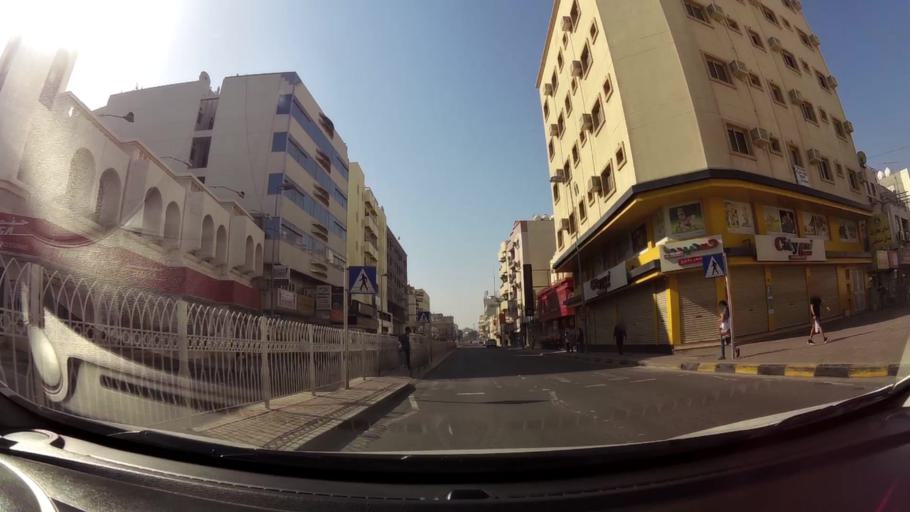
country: BH
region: Manama
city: Manama
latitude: 26.2292
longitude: 50.5881
